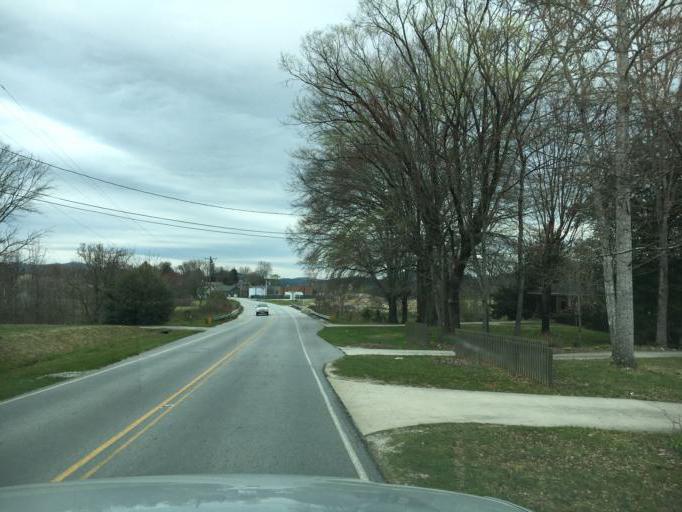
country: US
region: North Carolina
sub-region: Transylvania County
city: Brevard
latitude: 35.2338
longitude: -82.7209
